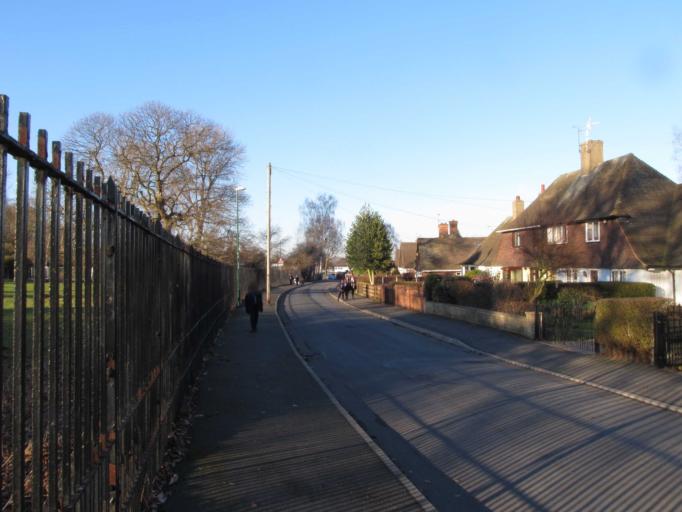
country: GB
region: England
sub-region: Nottingham
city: Nottingham
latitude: 52.9495
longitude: -1.1978
